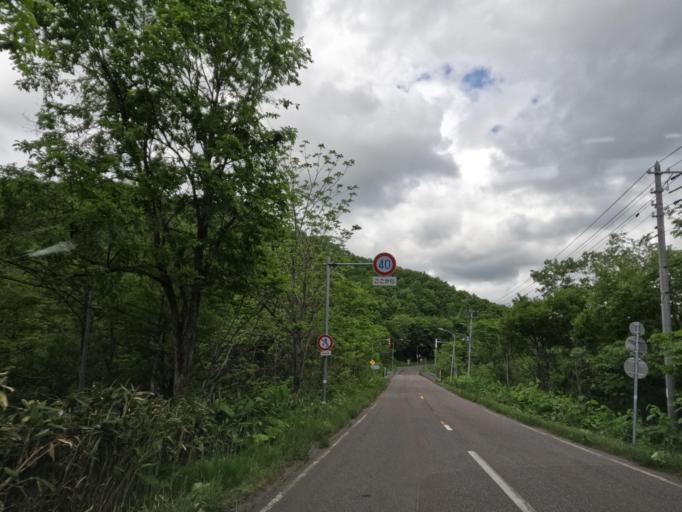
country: JP
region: Hokkaido
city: Takikawa
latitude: 43.5602
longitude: 141.6972
